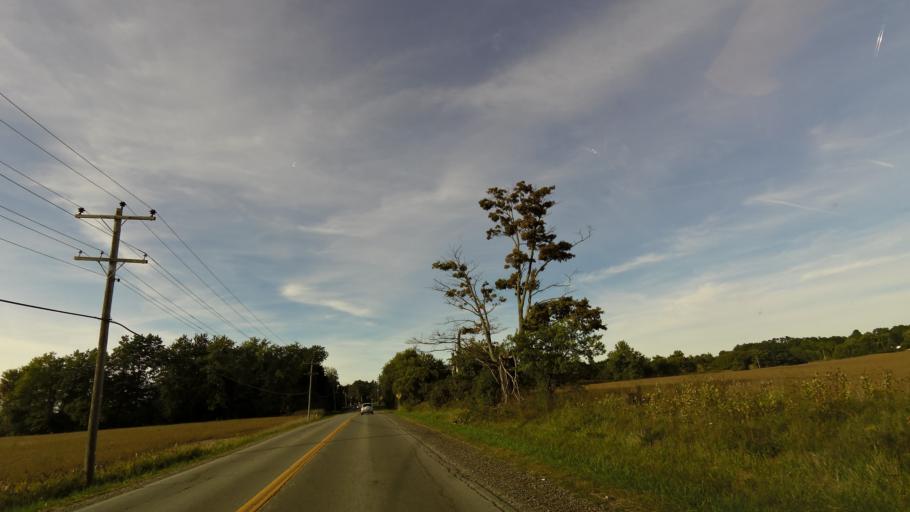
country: CA
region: Ontario
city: Ancaster
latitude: 43.1815
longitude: -79.9756
